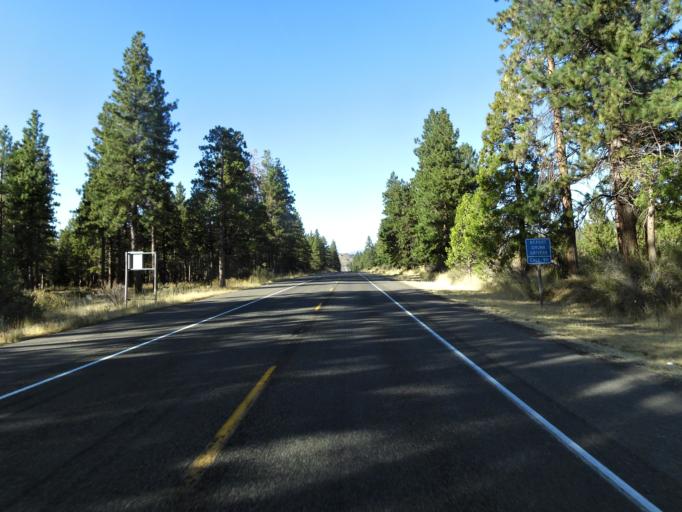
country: US
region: California
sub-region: Siskiyou County
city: Weed
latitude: 41.4591
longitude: -122.3568
